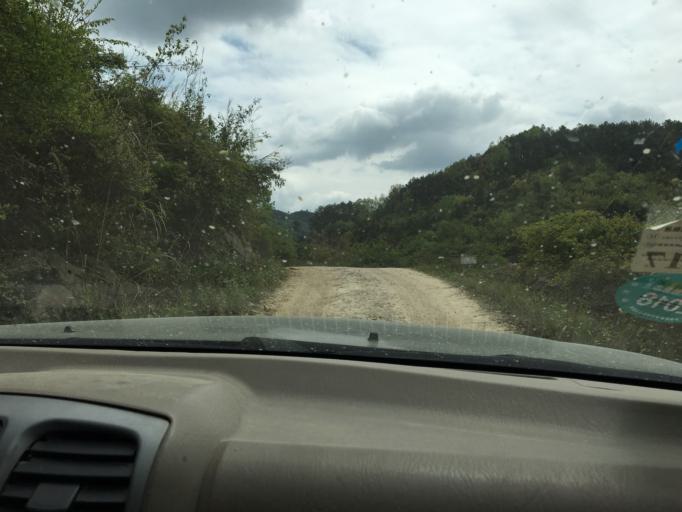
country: CN
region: Guizhou Sheng
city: Kuanping
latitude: 28.0202
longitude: 108.0747
